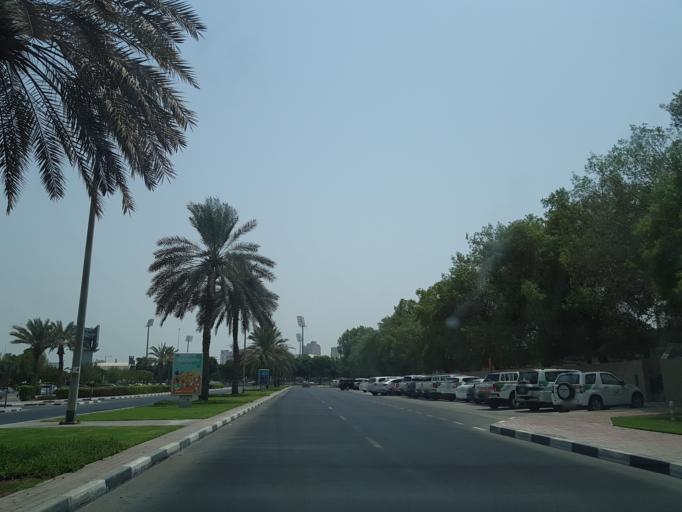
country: AE
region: Ash Shariqah
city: Sharjah
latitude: 25.2279
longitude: 55.3254
